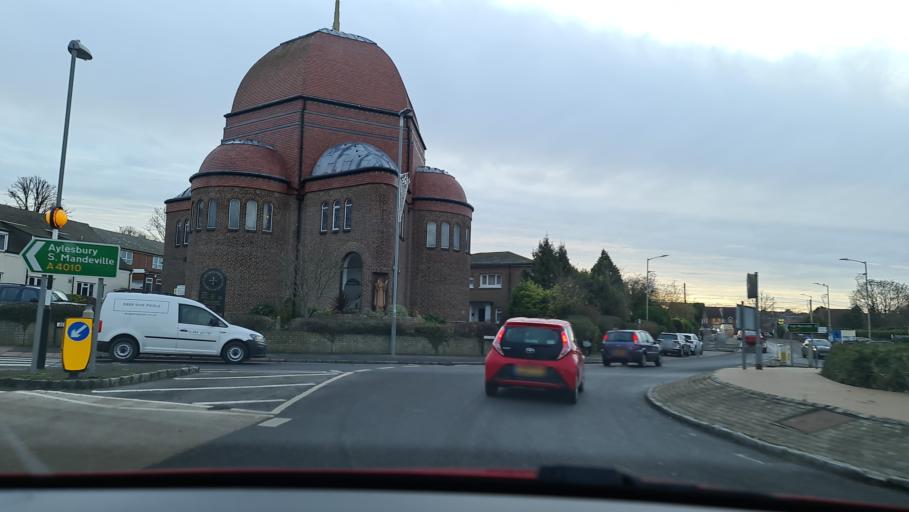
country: GB
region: England
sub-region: Buckinghamshire
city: Princes Risborough
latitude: 51.7259
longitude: -0.8325
